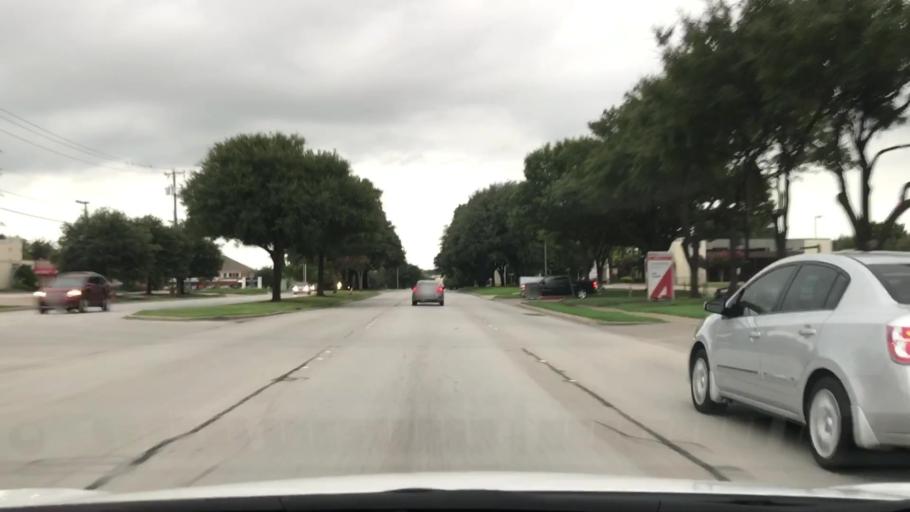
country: US
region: Texas
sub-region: Tarrant County
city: Watauga
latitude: 32.8598
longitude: -97.2901
